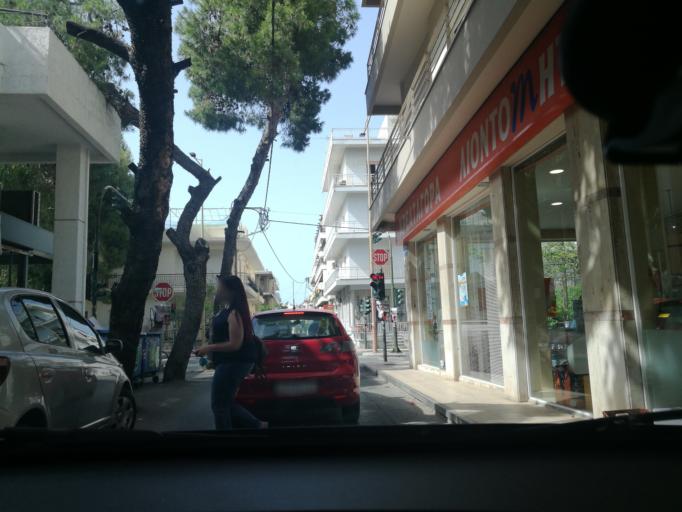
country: GR
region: Crete
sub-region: Nomos Irakleiou
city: Irakleion
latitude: 35.3266
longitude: 25.1305
